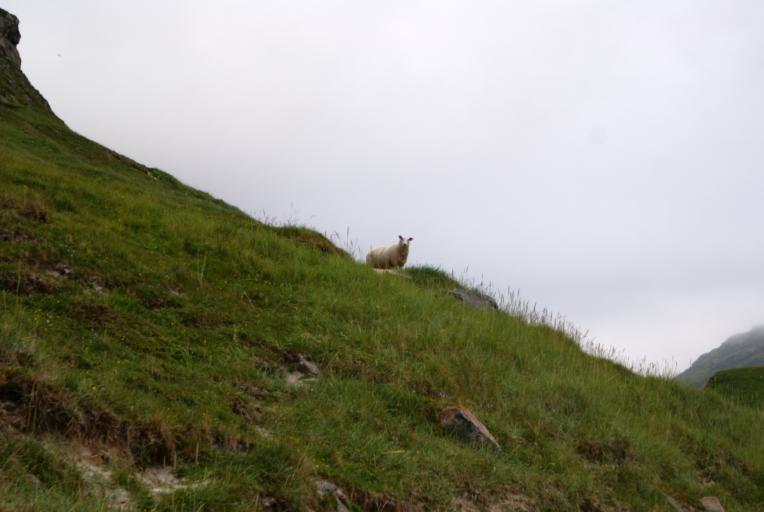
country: NO
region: Nordland
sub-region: Vestvagoy
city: Gravdal
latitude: 68.2001
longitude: 13.5245
